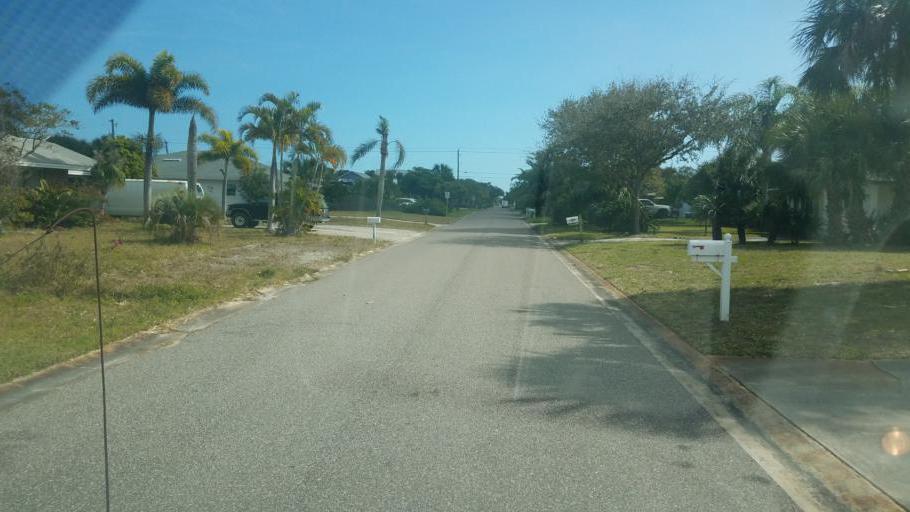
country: US
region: Florida
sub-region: Brevard County
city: Melbourne Beach
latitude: 28.0664
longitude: -80.5621
